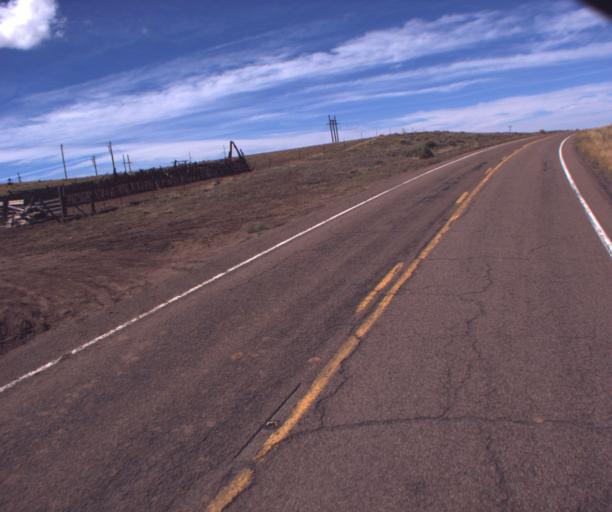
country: US
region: Arizona
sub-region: Apache County
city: Saint Johns
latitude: 34.4805
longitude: -109.6168
